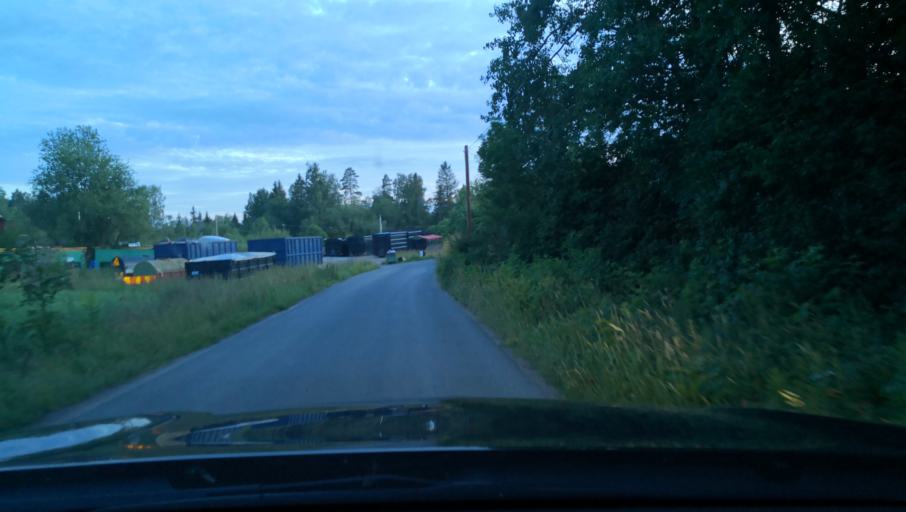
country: SE
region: Uppsala
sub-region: Osthammars Kommun
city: Bjorklinge
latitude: 60.0324
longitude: 17.4622
